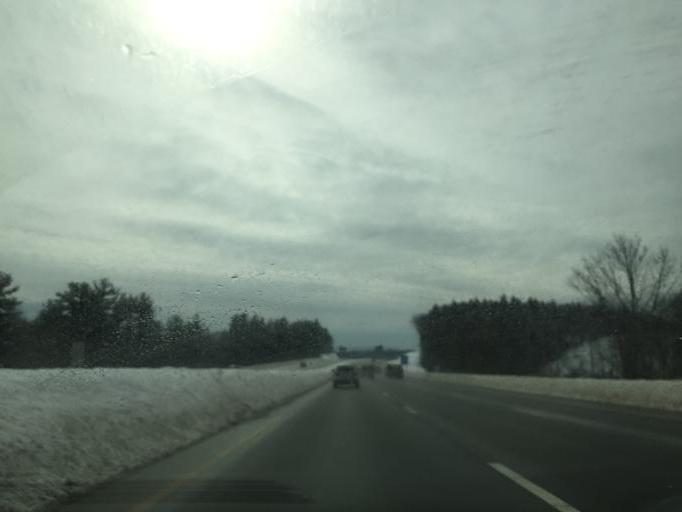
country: US
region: New Hampshire
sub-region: Strafford County
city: Rochester
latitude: 43.3044
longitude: -70.9949
